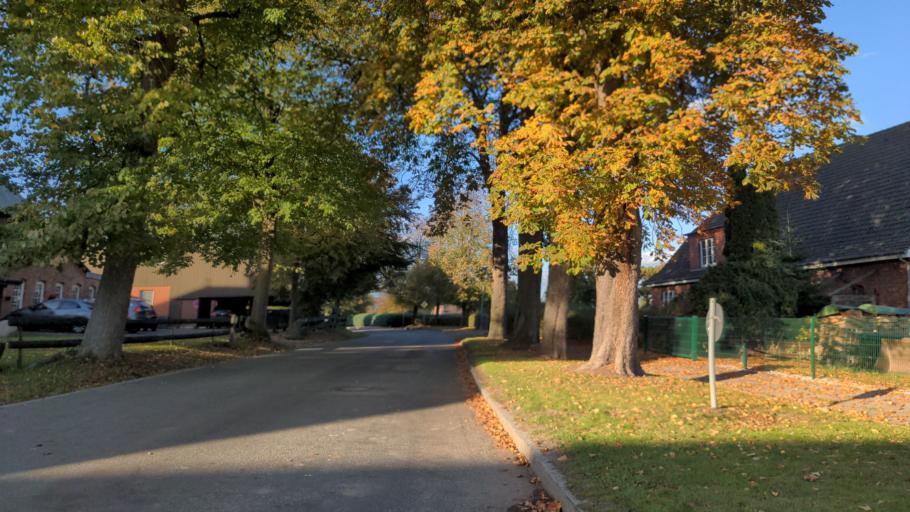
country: DE
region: Schleswig-Holstein
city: Monkhagen
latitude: 53.9476
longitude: 10.5281
